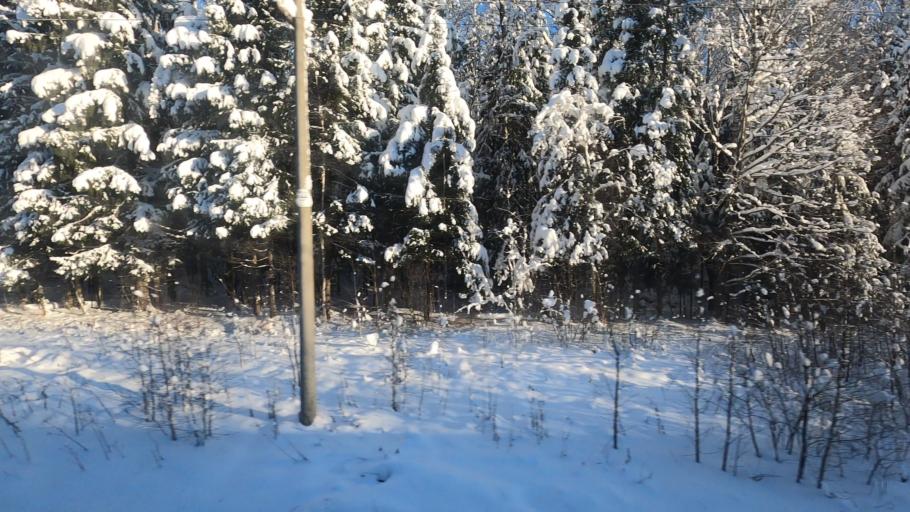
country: RU
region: Moskovskaya
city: Novo-Nikol'skoye
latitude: 56.6197
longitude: 37.5657
